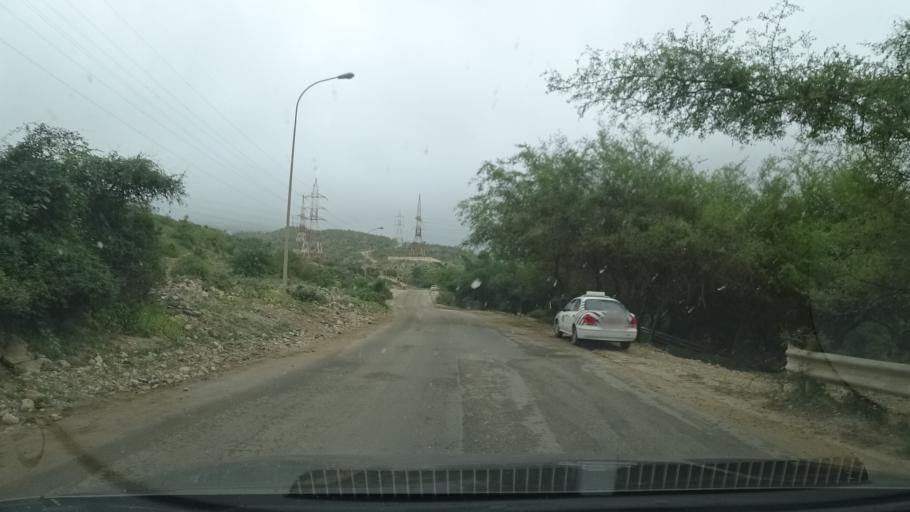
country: OM
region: Zufar
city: Salalah
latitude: 17.0951
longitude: 54.0782
